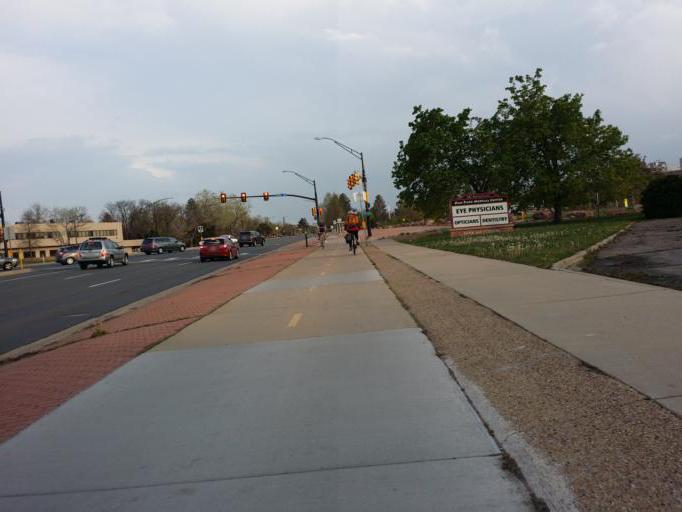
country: US
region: Colorado
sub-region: Boulder County
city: Boulder
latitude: 39.9969
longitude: -105.2616
